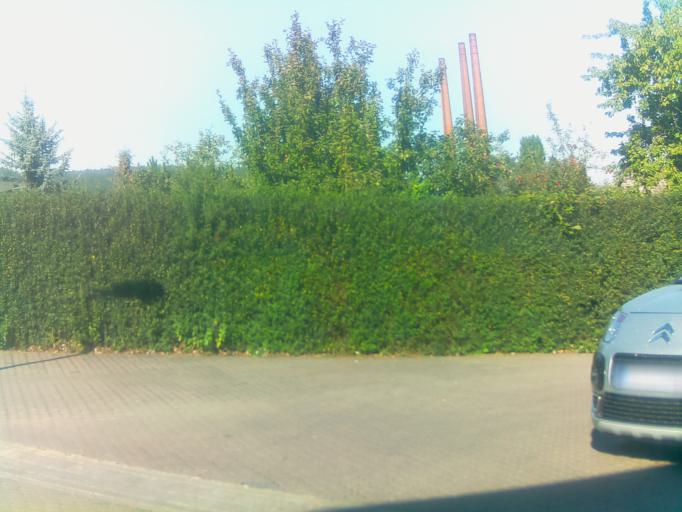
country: DE
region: Thuringia
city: Kahla
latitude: 50.8094
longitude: 11.5776
